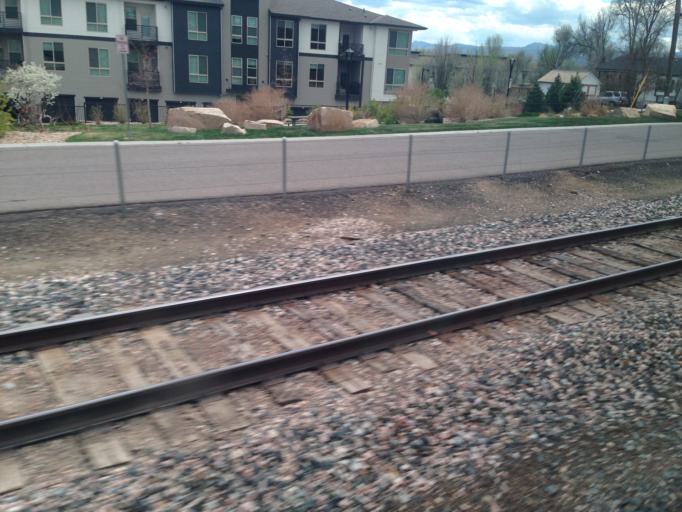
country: US
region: Colorado
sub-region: Jefferson County
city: Arvada
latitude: 39.8001
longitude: -105.0737
